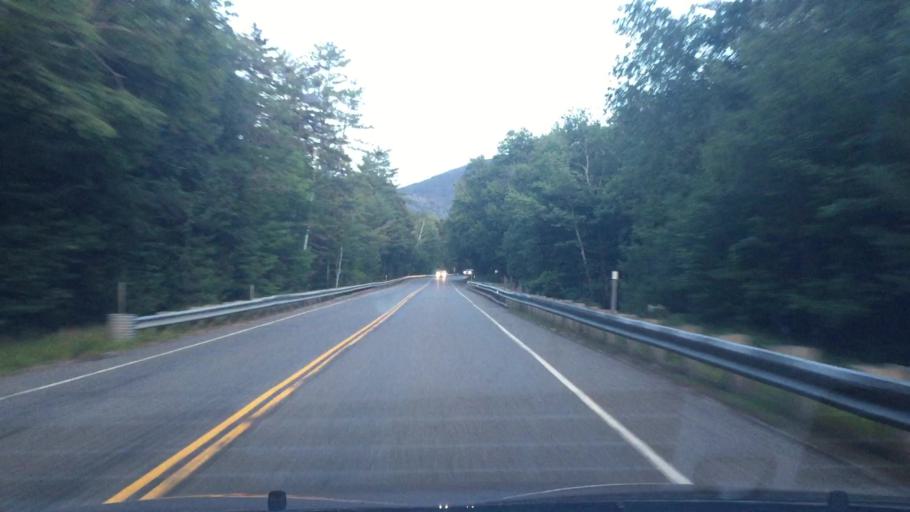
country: US
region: New Hampshire
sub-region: Grafton County
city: Woodstock
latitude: 44.0360
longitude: -71.5303
